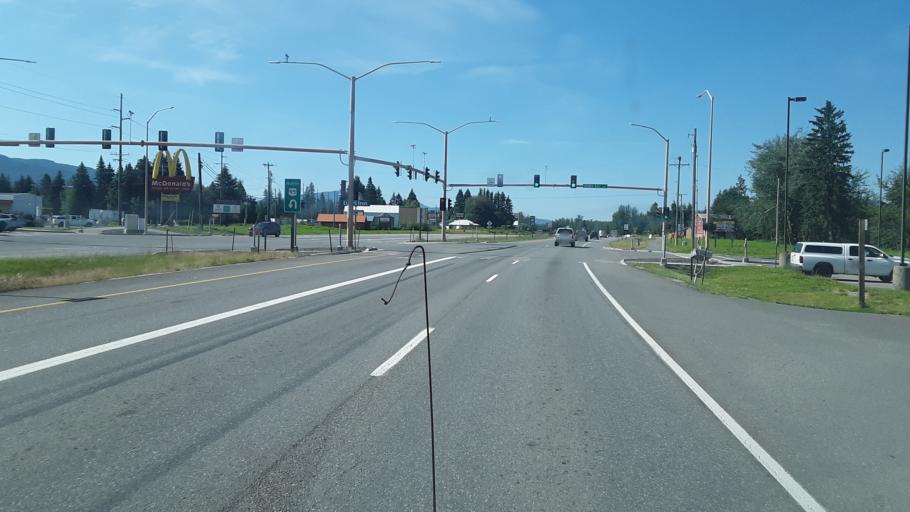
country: US
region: Idaho
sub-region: Bonner County
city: Ponderay
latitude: 48.3018
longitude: -116.5466
